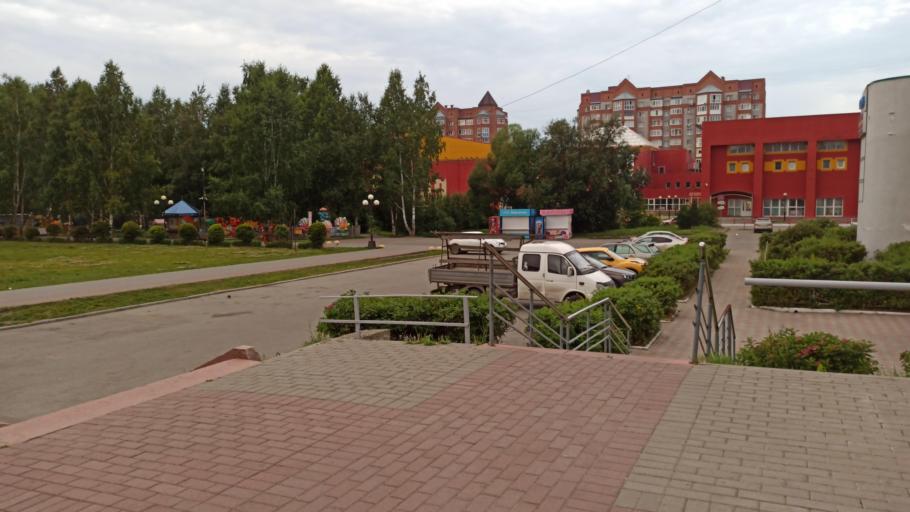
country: RU
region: Tomsk
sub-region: Tomskiy Rayon
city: Tomsk
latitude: 56.4615
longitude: 84.9714
